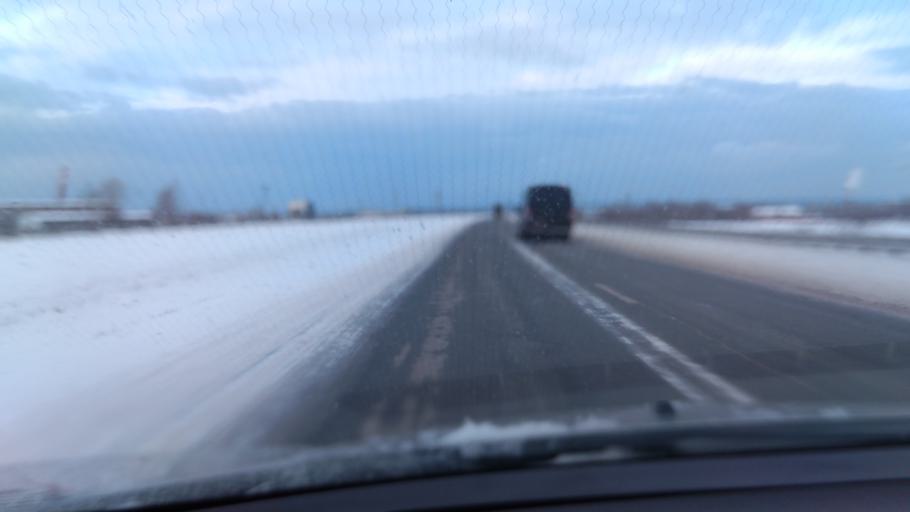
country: RU
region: Sverdlovsk
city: Tsementnyy
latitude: 57.4714
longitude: 60.1820
